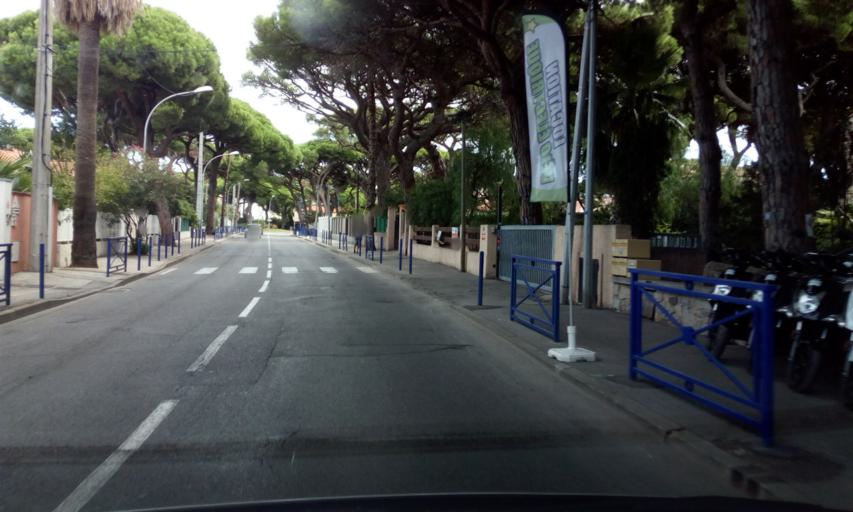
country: FR
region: Provence-Alpes-Cote d'Azur
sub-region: Departement du Var
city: Hyeres
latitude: 43.0822
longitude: 6.1518
